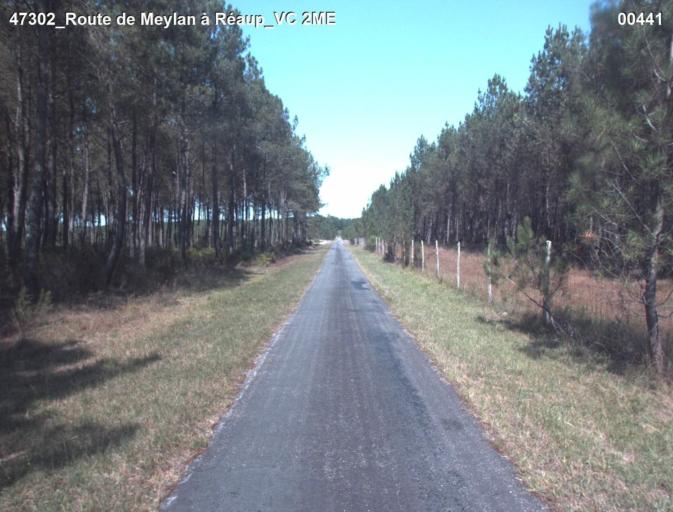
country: FR
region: Aquitaine
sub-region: Departement du Lot-et-Garonne
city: Mezin
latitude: 44.1042
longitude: 0.1383
